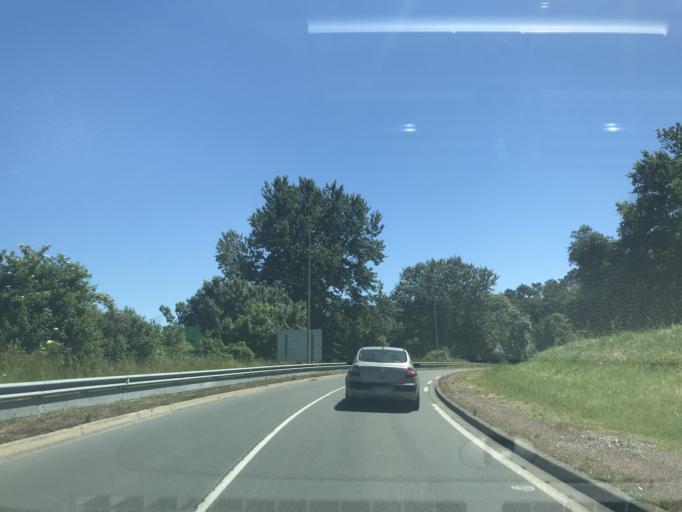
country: FR
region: Poitou-Charentes
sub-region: Departement de la Charente-Maritime
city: Saint-Georges-de-Didonne
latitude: 45.5961
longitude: -0.9743
